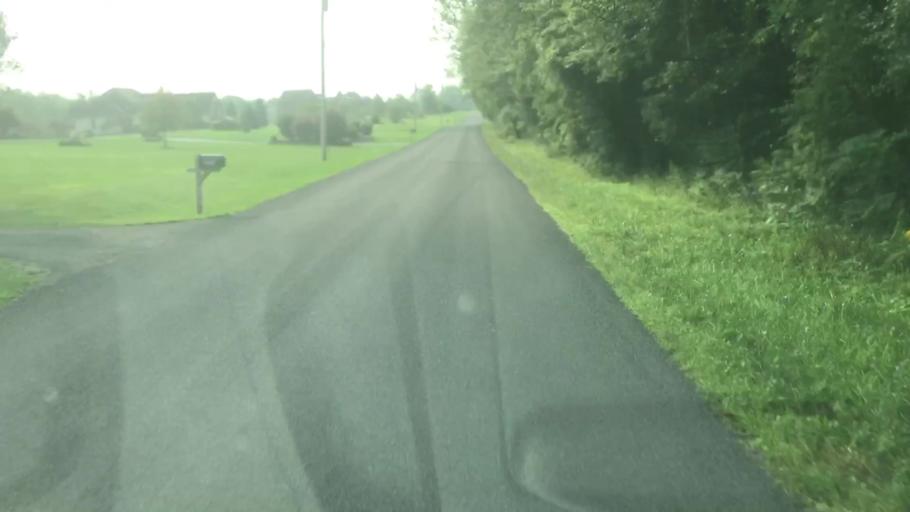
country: US
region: New York
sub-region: Onondaga County
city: Skaneateles
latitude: 42.9118
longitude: -76.4553
